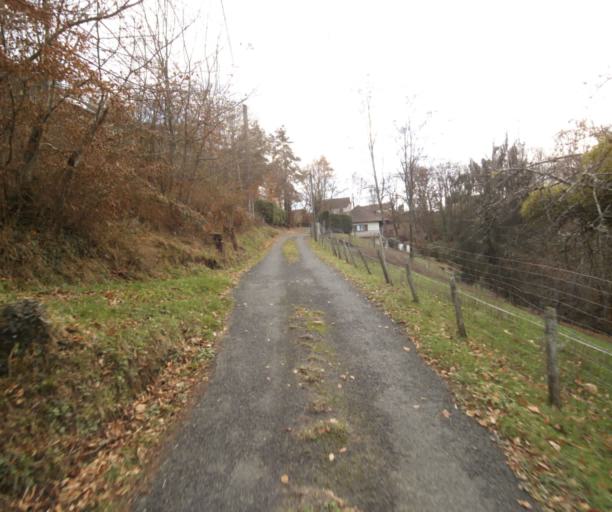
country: FR
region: Limousin
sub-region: Departement de la Correze
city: Laguenne
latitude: 45.2361
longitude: 1.7857
